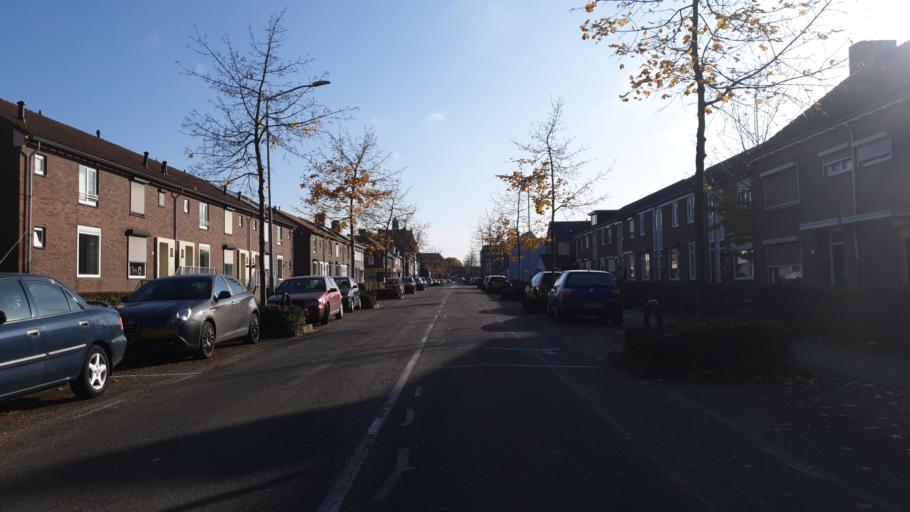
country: NL
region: Limburg
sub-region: Gemeente Venlo
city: Venlo
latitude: 51.3811
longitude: 6.1792
